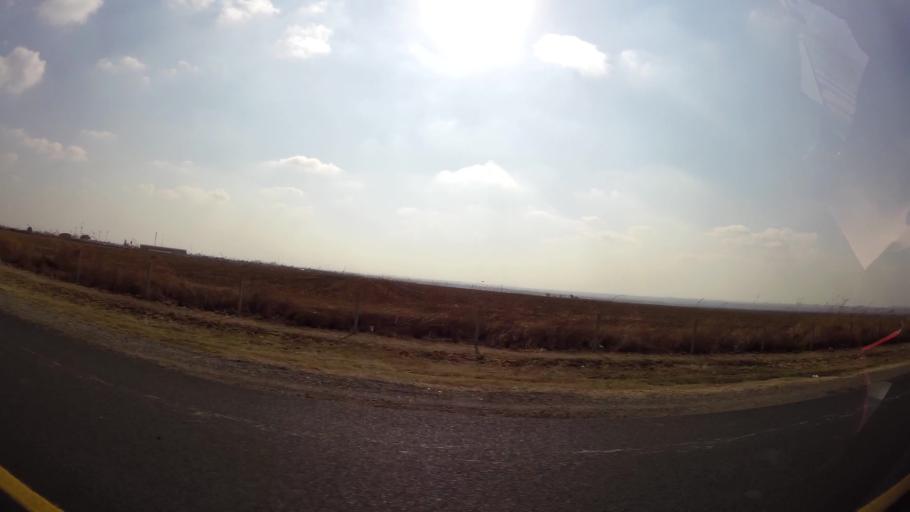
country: ZA
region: Gauteng
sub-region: Ekurhuleni Metropolitan Municipality
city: Springs
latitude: -26.1574
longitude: 28.4299
